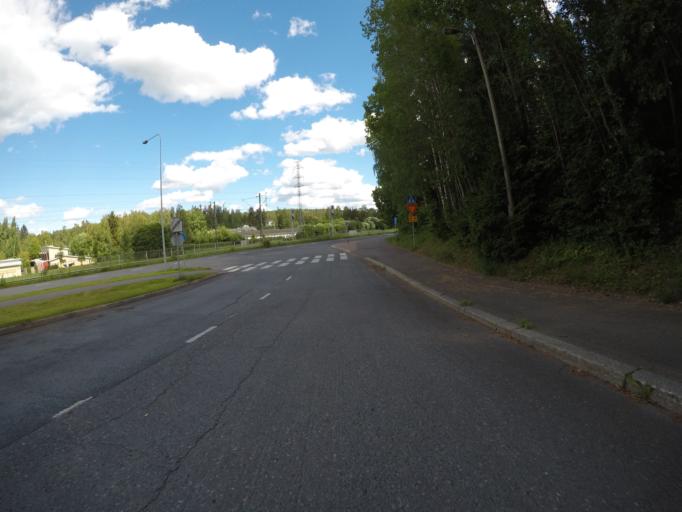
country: FI
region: Haeme
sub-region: Haemeenlinna
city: Haemeenlinna
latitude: 61.0173
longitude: 24.4351
